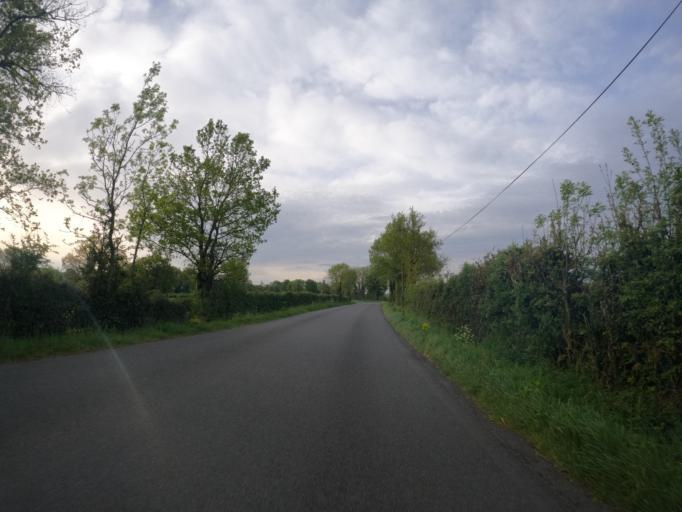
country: FR
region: Poitou-Charentes
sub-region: Departement des Deux-Sevres
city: La Chapelle-Saint-Laurent
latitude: 46.6972
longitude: -0.5173
